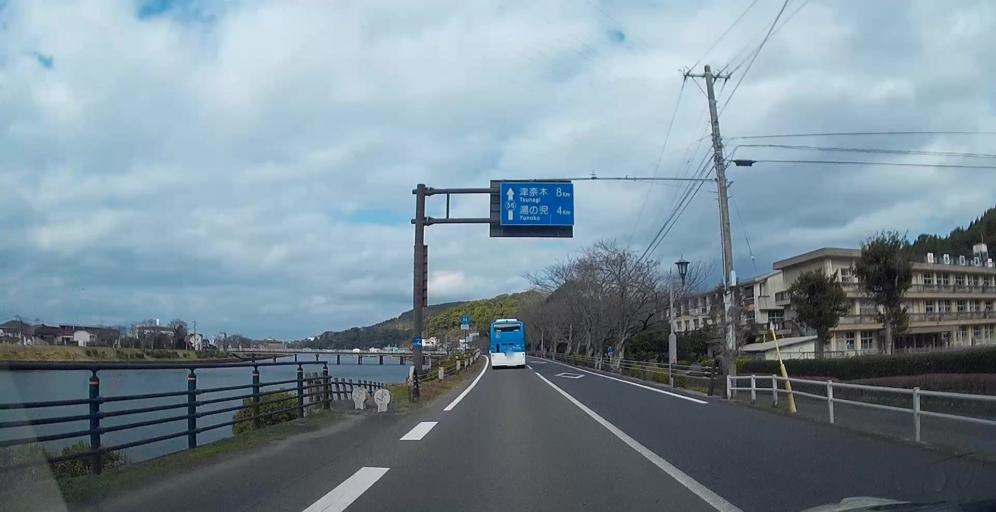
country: JP
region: Kumamoto
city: Minamata
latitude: 32.2122
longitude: 130.4080
